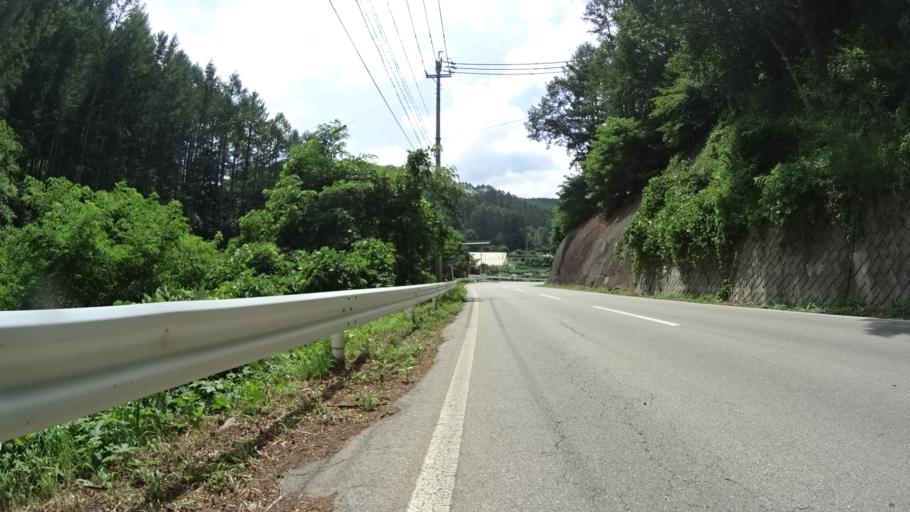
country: JP
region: Nagano
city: Saku
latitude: 36.0606
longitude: 138.5095
